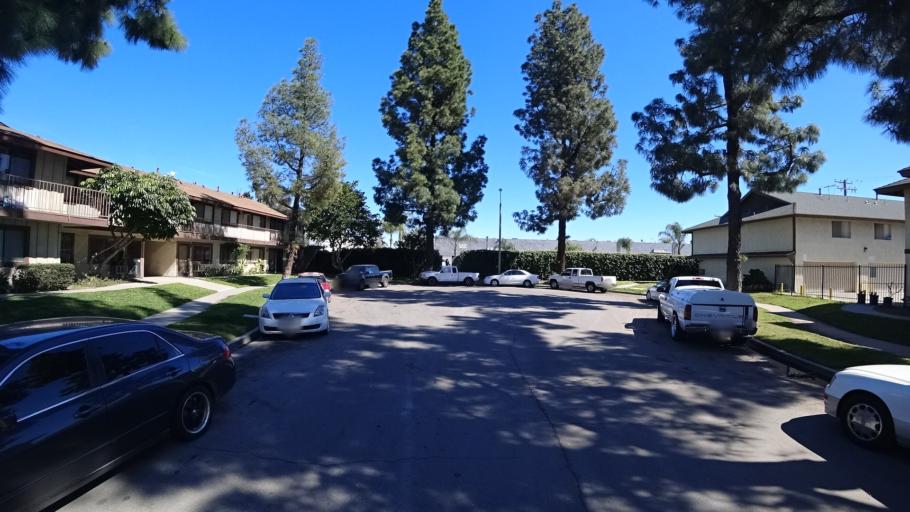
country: US
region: California
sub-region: Orange County
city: Anaheim
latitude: 33.8238
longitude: -117.9174
